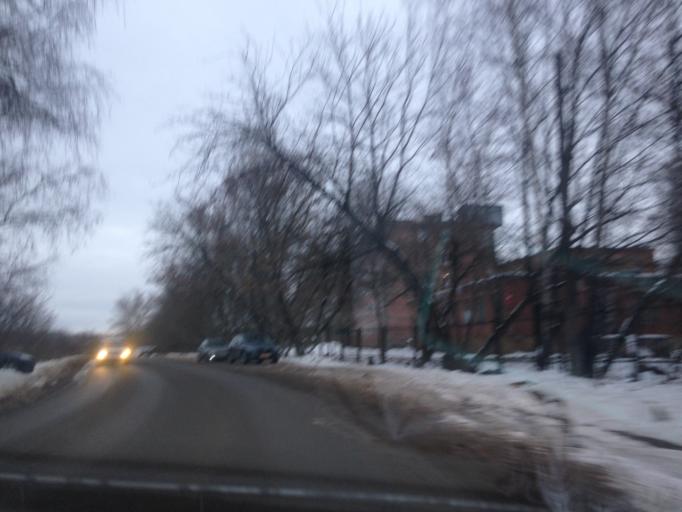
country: RU
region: Tula
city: Shchekino
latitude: 54.0209
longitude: 37.5151
